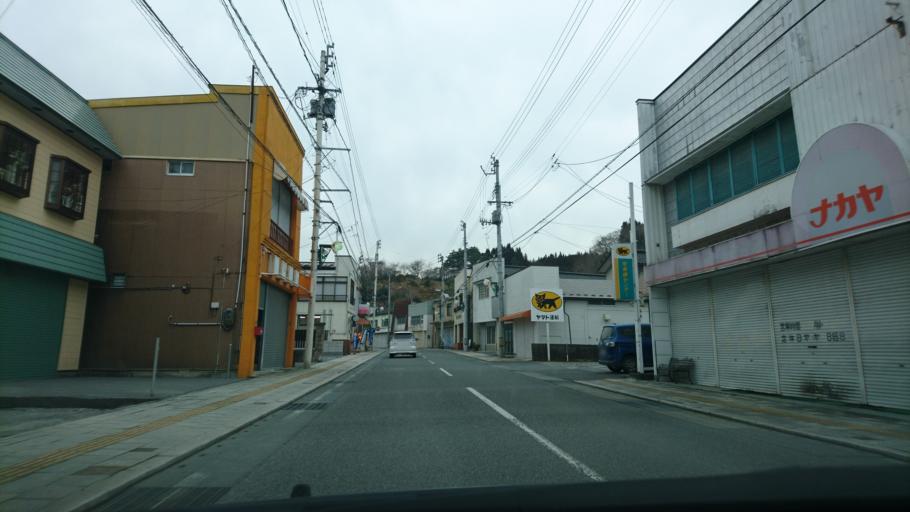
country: JP
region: Iwate
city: Ofunato
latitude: 39.1415
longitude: 141.5791
